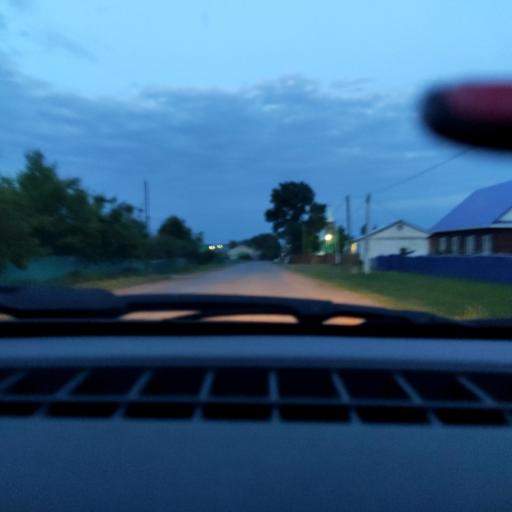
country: RU
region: Bashkortostan
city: Tolbazy
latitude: 54.2935
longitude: 55.8103
